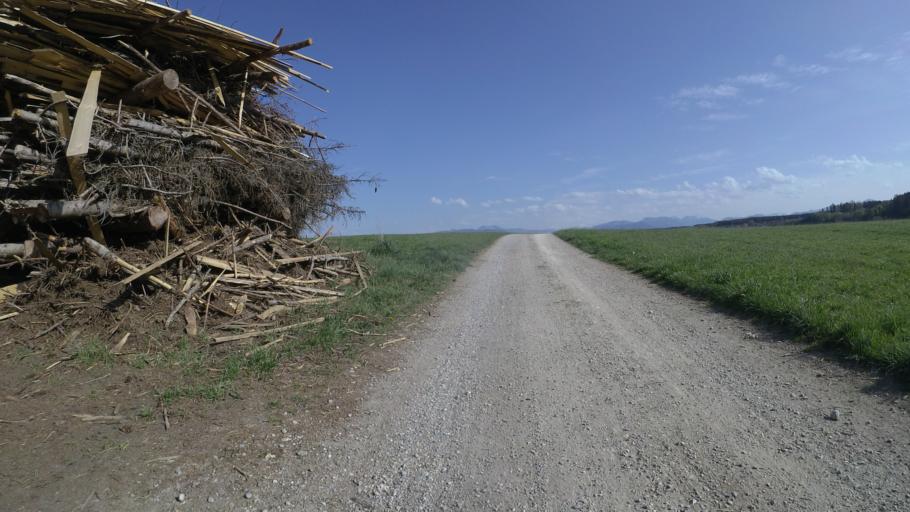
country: DE
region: Bavaria
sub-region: Upper Bavaria
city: Nussdorf
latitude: 47.9243
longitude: 12.6073
